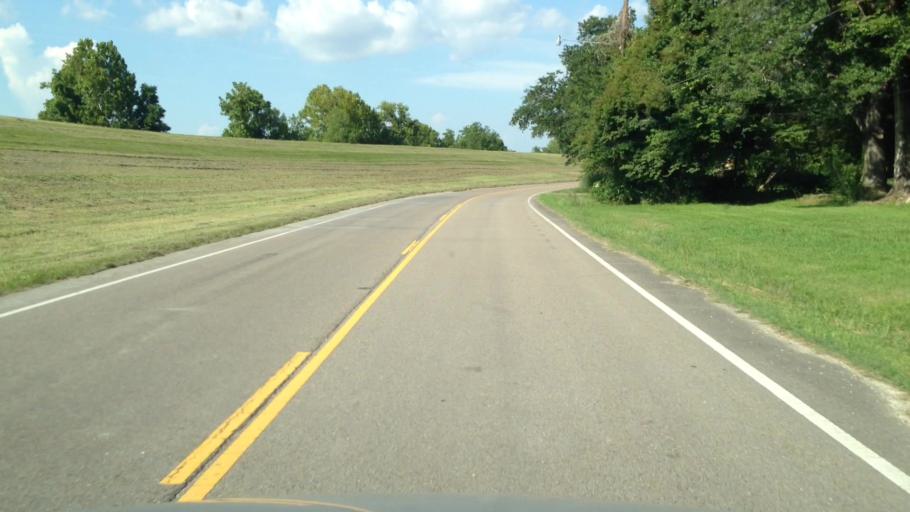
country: US
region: Louisiana
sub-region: Jefferson Parish
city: Jefferson
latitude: 29.9481
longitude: -90.1579
